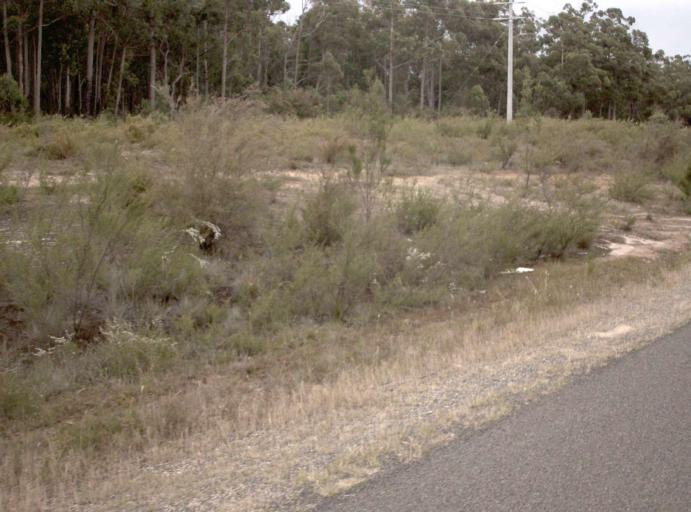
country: AU
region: Victoria
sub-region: East Gippsland
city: Lakes Entrance
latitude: -37.7212
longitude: 147.9566
